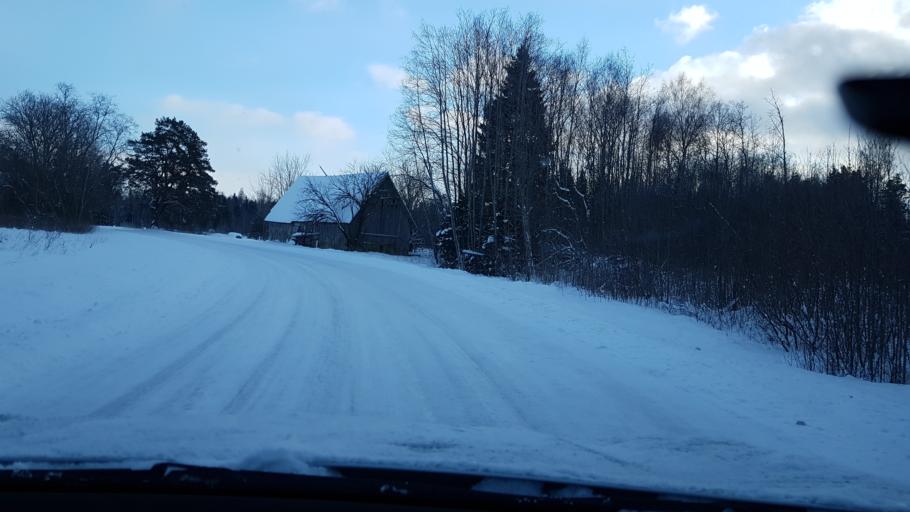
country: EE
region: Harju
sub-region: Nissi vald
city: Turba
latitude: 59.1529
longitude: 24.1454
